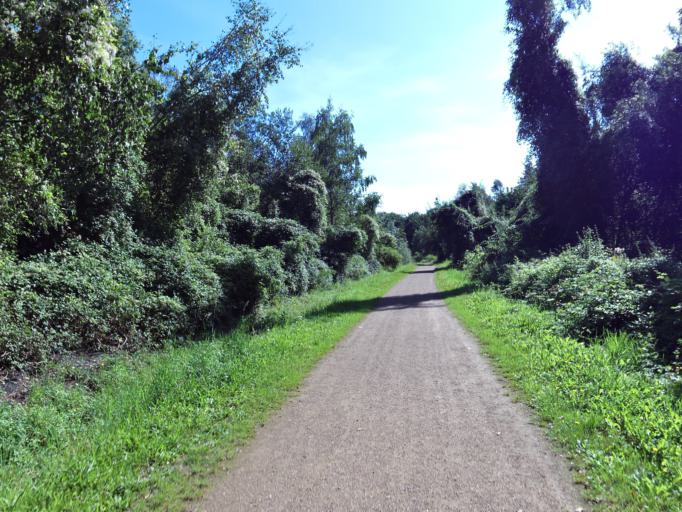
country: DE
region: North Rhine-Westphalia
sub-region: Regierungsbezirk Koln
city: Herzogenrath
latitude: 50.8896
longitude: 6.1083
